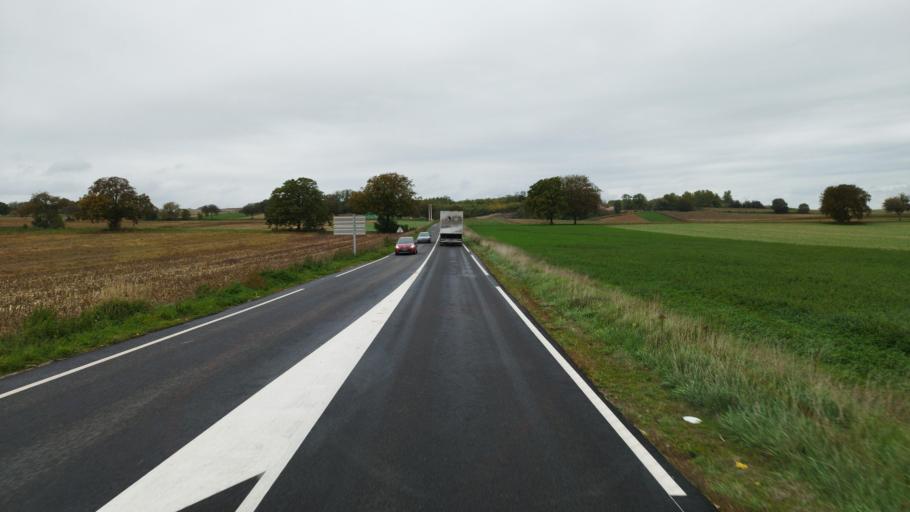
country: FR
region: Alsace
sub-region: Departement du Bas-Rhin
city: Seltz
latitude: 48.9138
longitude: 8.1050
